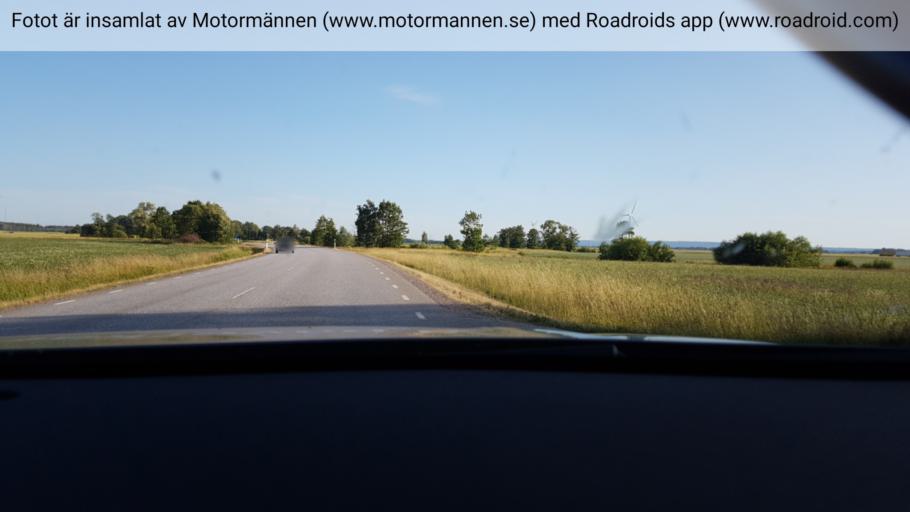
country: SE
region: Vaestra Goetaland
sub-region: Toreboda Kommun
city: Toereboda
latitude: 58.6162
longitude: 14.0111
